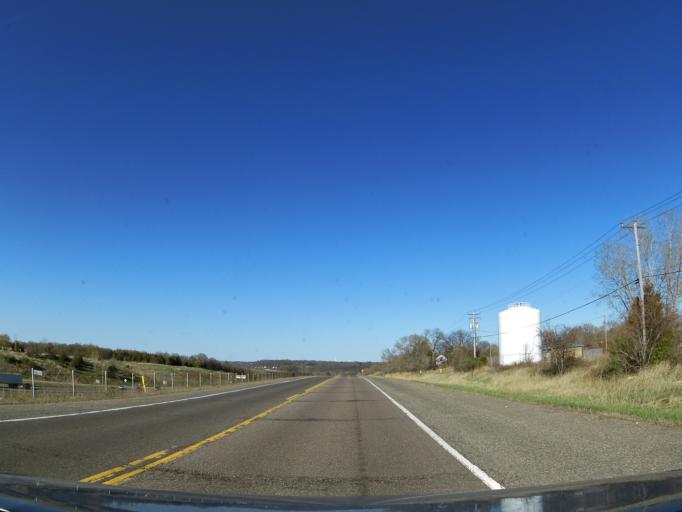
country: US
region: Minnesota
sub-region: Washington County
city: Lakeland
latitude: 44.9576
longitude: -92.7849
